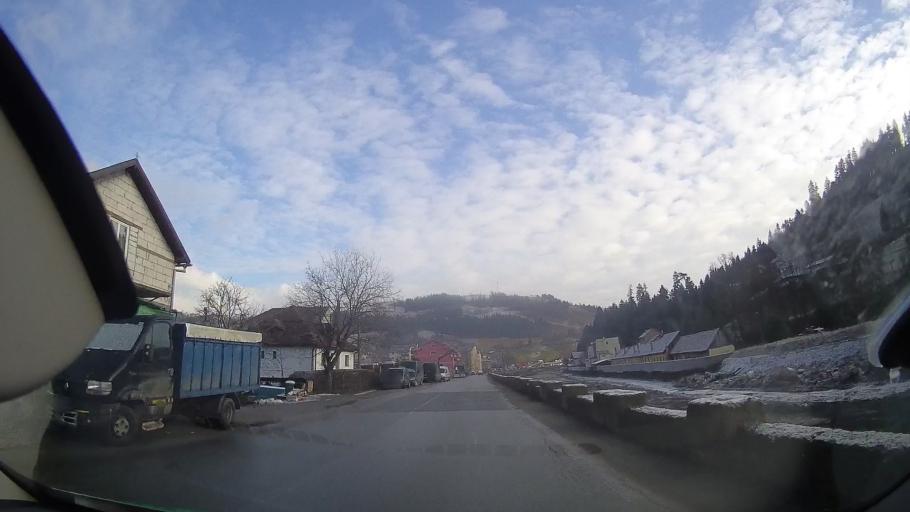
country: RO
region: Alba
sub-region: Oras Campeni
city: Campeni
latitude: 46.3608
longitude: 23.0471
